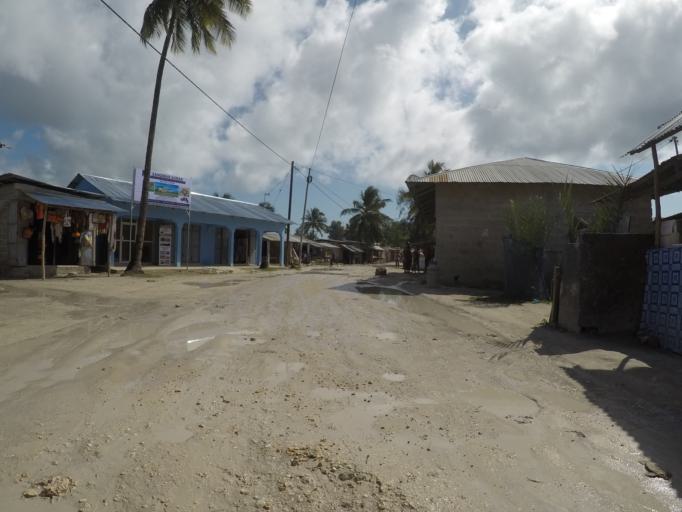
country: TZ
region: Zanzibar North
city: Nungwi
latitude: -5.7276
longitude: 39.2951
